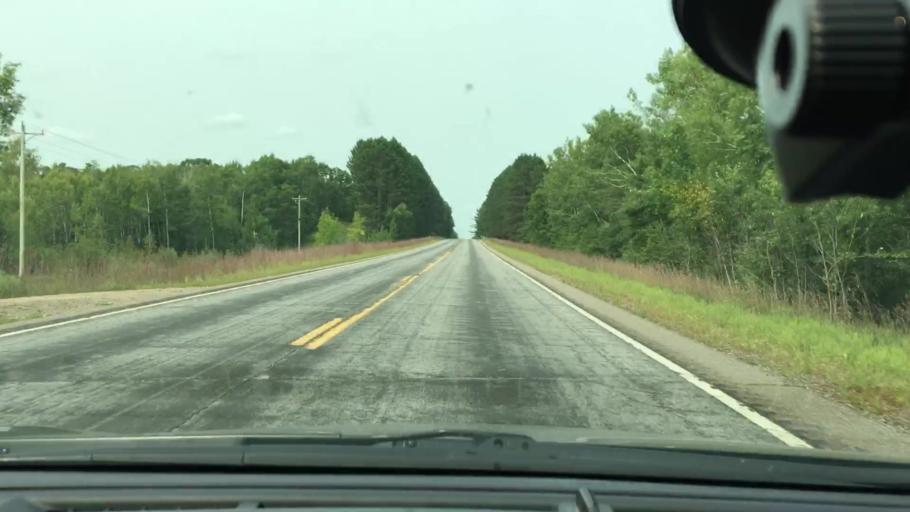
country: US
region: Minnesota
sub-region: Crow Wing County
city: Cross Lake
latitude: 46.7727
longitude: -93.9663
